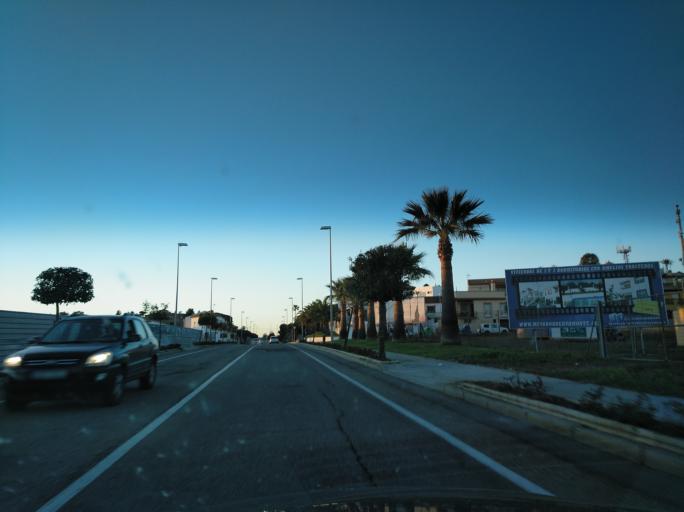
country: ES
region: Andalusia
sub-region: Provincia de Huelva
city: Ayamonte
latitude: 37.2238
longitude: -7.4020
